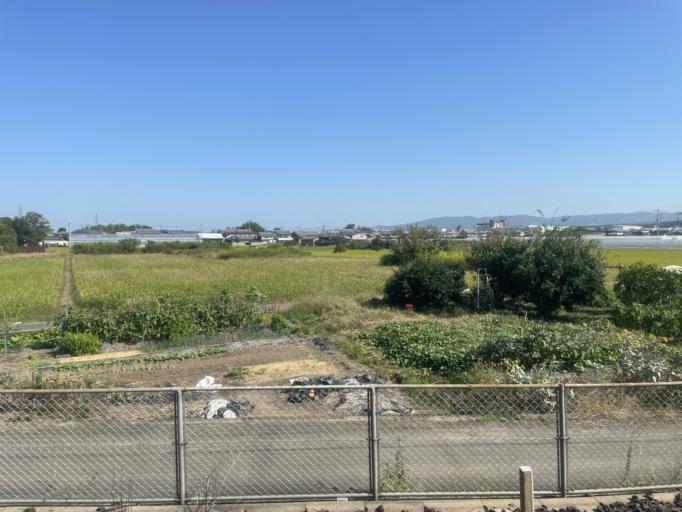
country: JP
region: Nara
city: Tenri
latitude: 34.6034
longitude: 135.7903
